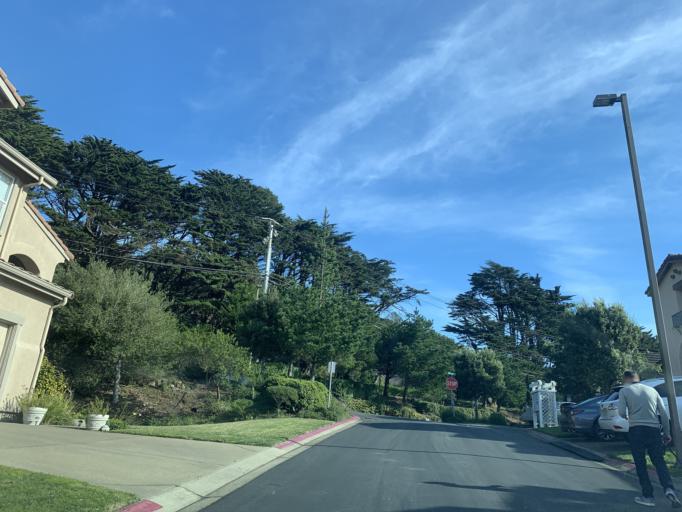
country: US
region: California
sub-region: San Mateo County
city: Pacifica
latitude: 37.6404
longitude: -122.4671
